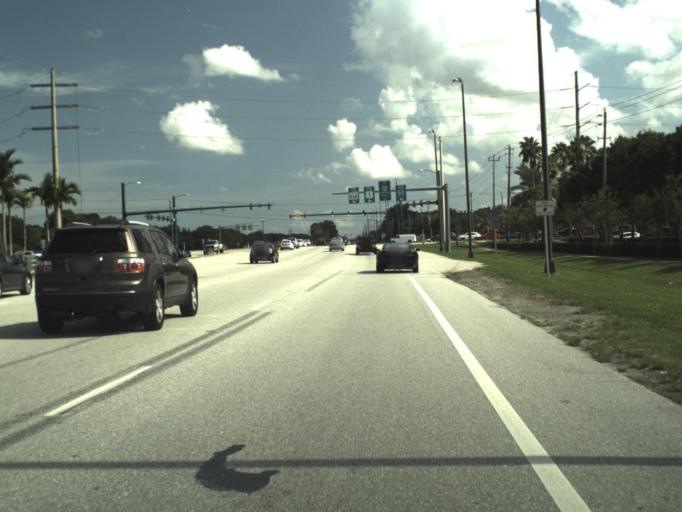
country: US
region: Florida
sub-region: Palm Beach County
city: Boca Pointe
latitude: 26.3513
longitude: -80.2035
